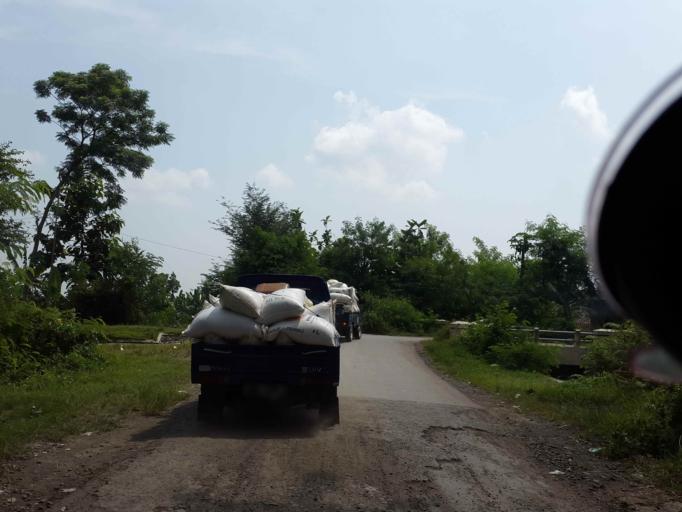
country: ID
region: Central Java
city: Pemalang
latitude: -6.9471
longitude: 109.3492
